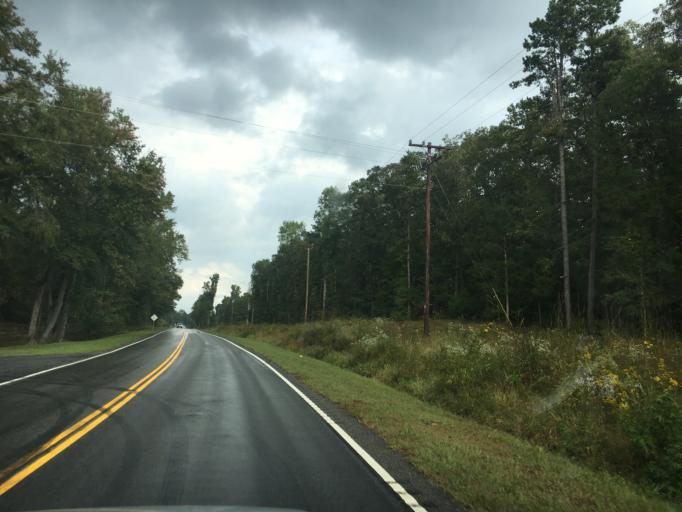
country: US
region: South Carolina
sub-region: Anderson County
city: Homeland Park
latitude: 34.4118
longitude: -82.7843
